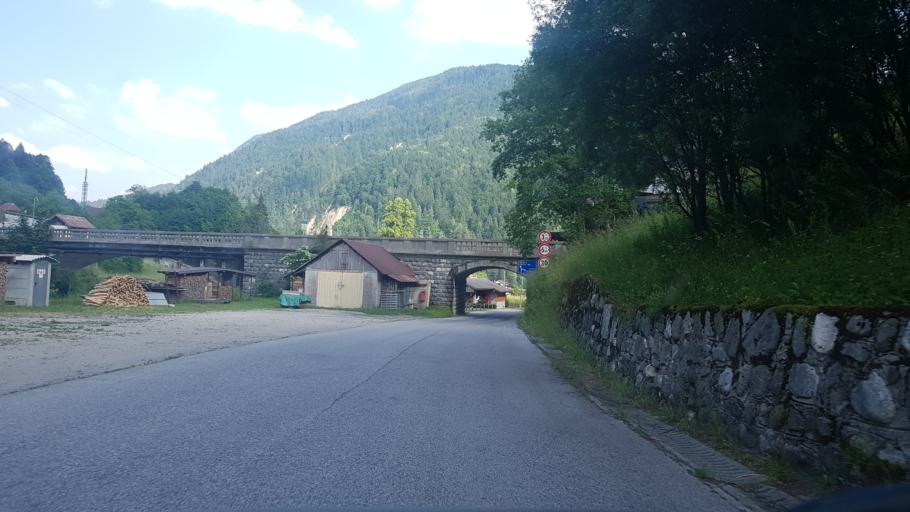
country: IT
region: Friuli Venezia Giulia
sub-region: Provincia di Udine
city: Pontebba
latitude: 46.5108
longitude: 13.2989
